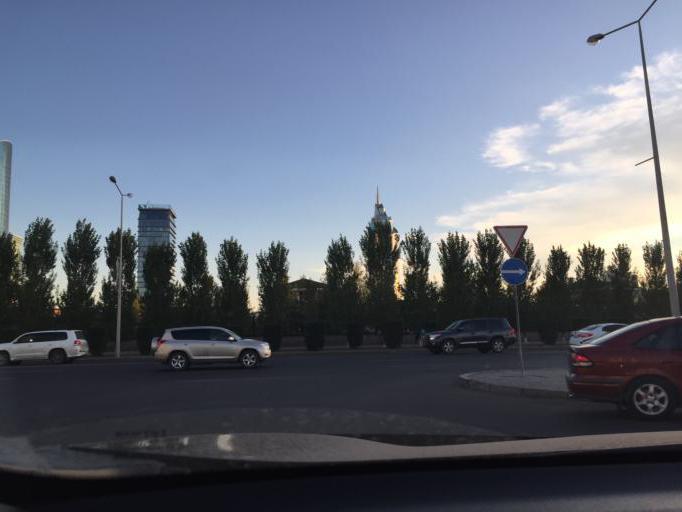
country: KZ
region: Astana Qalasy
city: Astana
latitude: 51.1361
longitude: 71.4201
